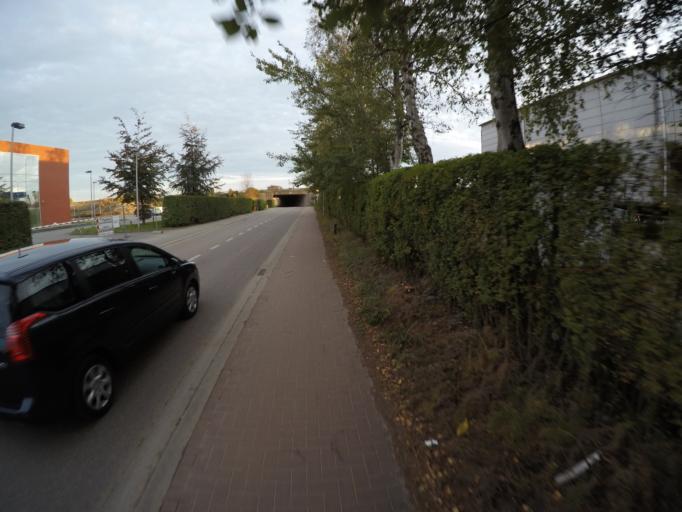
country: BE
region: Flanders
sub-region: Provincie Antwerpen
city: Zwijndrecht
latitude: 51.2122
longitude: 4.3427
